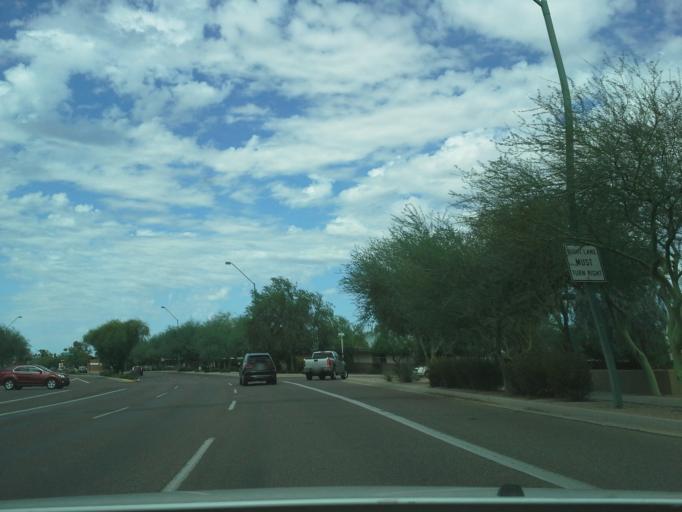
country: US
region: Arizona
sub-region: Maricopa County
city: Paradise Valley
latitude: 33.6256
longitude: -111.9401
